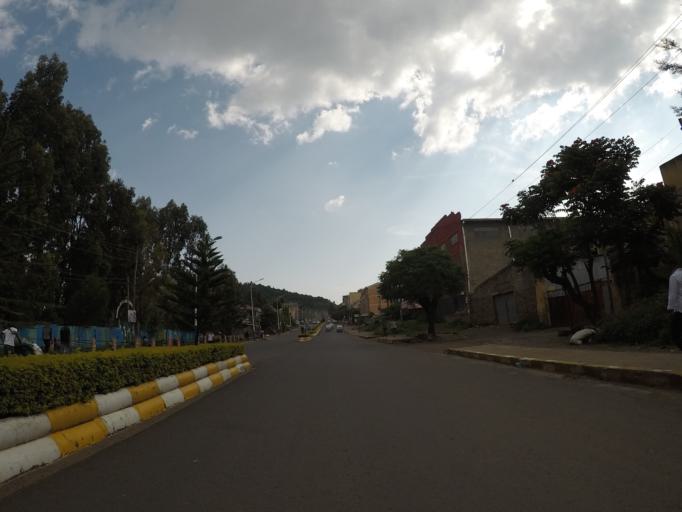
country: ET
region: Amhara
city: Gondar
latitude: 12.5955
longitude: 37.4485
